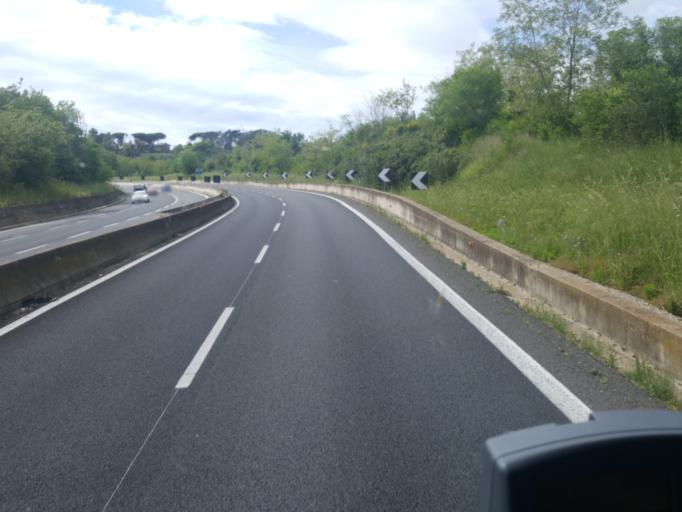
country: IT
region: Latium
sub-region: Citta metropolitana di Roma Capitale
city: Ara Nova
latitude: 41.9088
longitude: 12.2616
